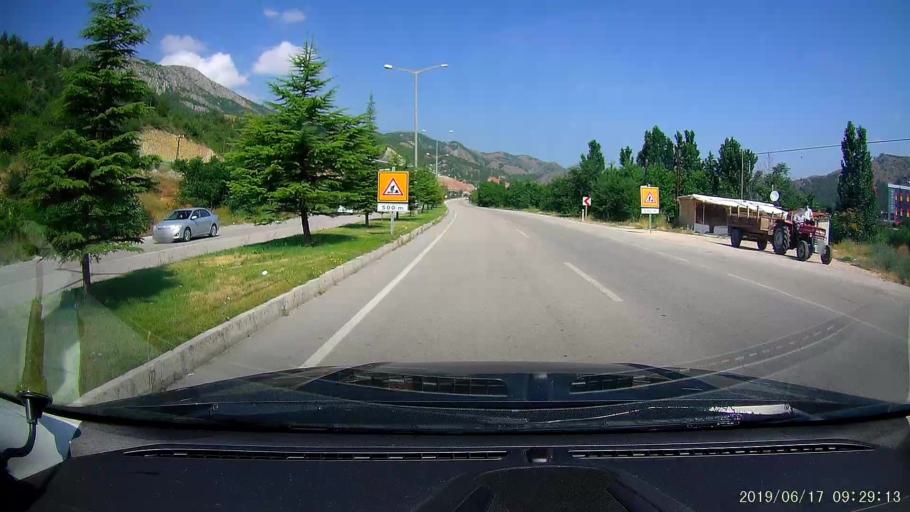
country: TR
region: Amasya
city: Amasya
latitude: 40.6950
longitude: 35.8148
